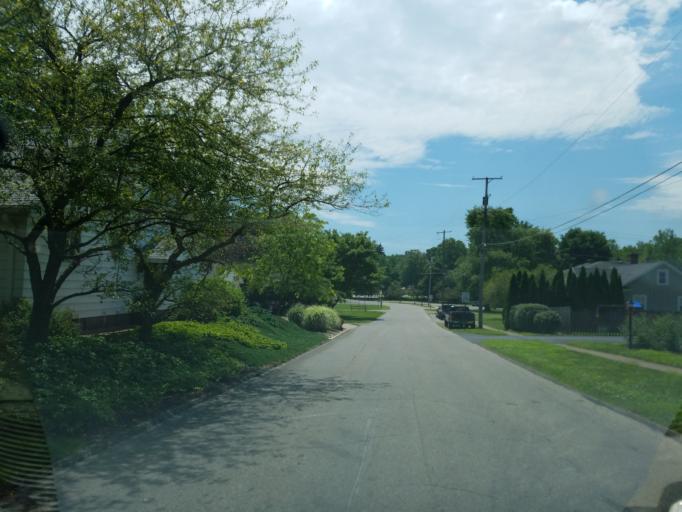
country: US
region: Ohio
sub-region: Ashland County
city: Ashland
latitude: 40.8754
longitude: -82.3293
